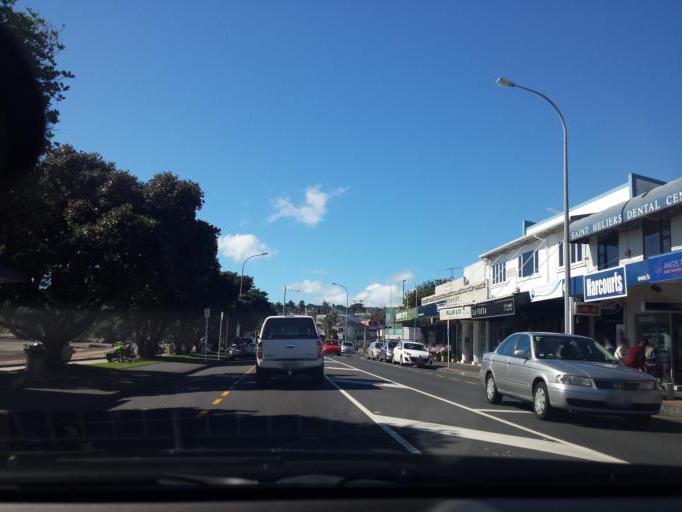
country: NZ
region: Auckland
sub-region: Auckland
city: Tamaki
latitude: -36.8502
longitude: 174.8575
